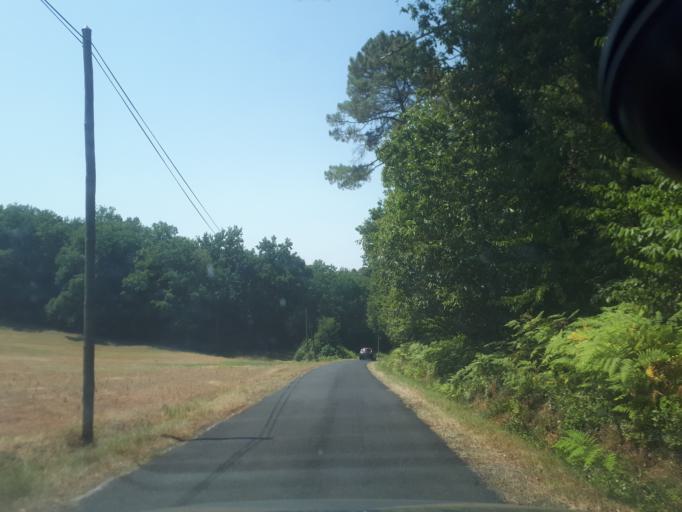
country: FR
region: Midi-Pyrenees
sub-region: Departement du Lot
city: Gourdon
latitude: 44.7363
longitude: 1.3203
